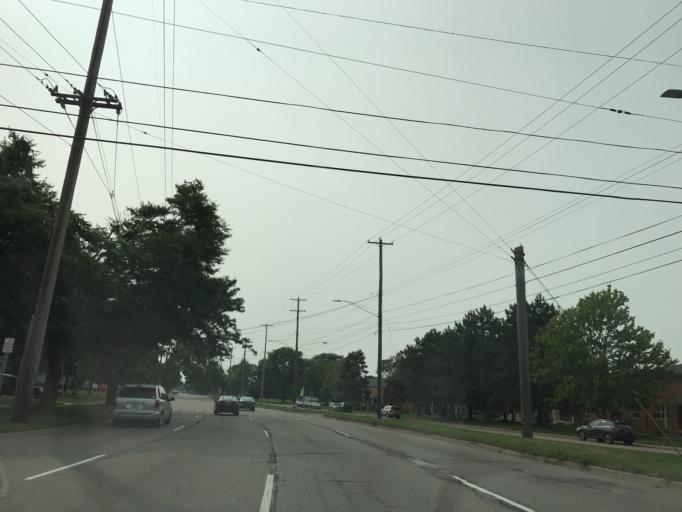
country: US
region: Michigan
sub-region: Ingham County
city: East Lansing
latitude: 42.7432
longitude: -84.5128
